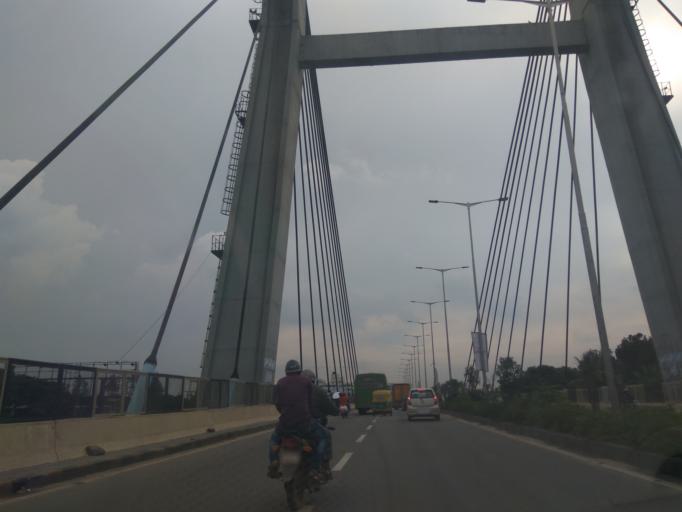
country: IN
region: Karnataka
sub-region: Bangalore Urban
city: Bangalore
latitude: 13.0011
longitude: 77.6783
